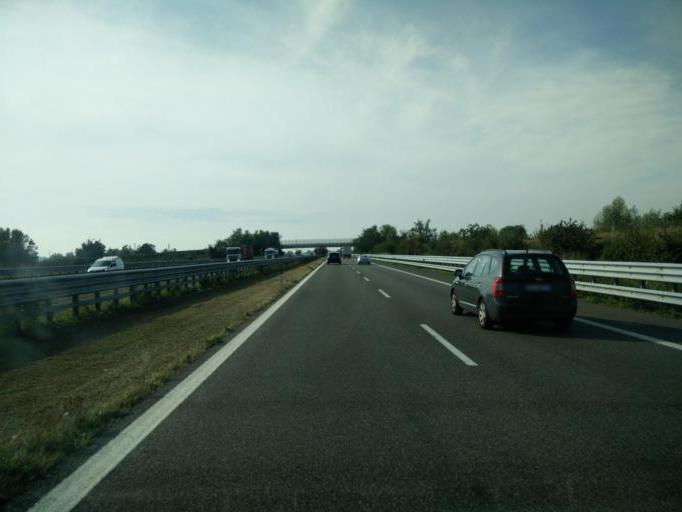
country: IT
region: Lombardy
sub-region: Provincia di Cremona
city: San Felice
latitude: 45.1668
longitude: 10.0819
